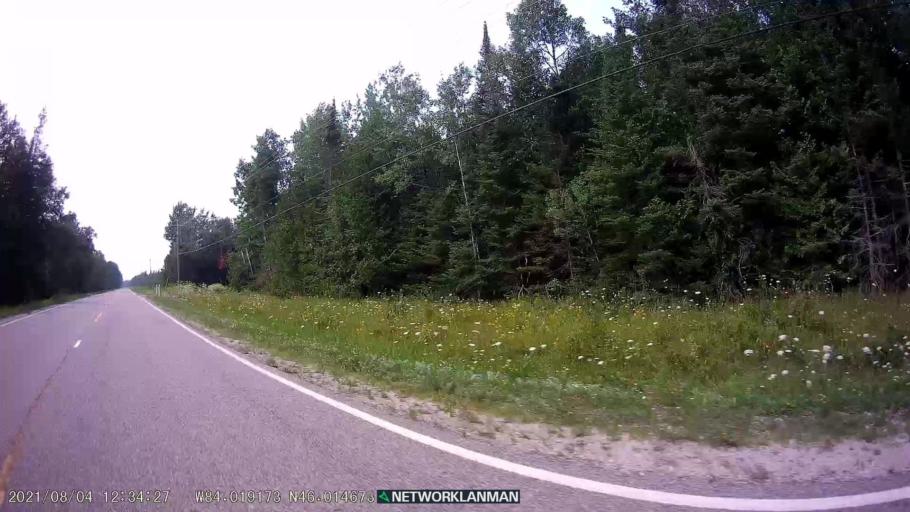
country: CA
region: Ontario
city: Thessalon
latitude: 46.0147
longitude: -84.0199
